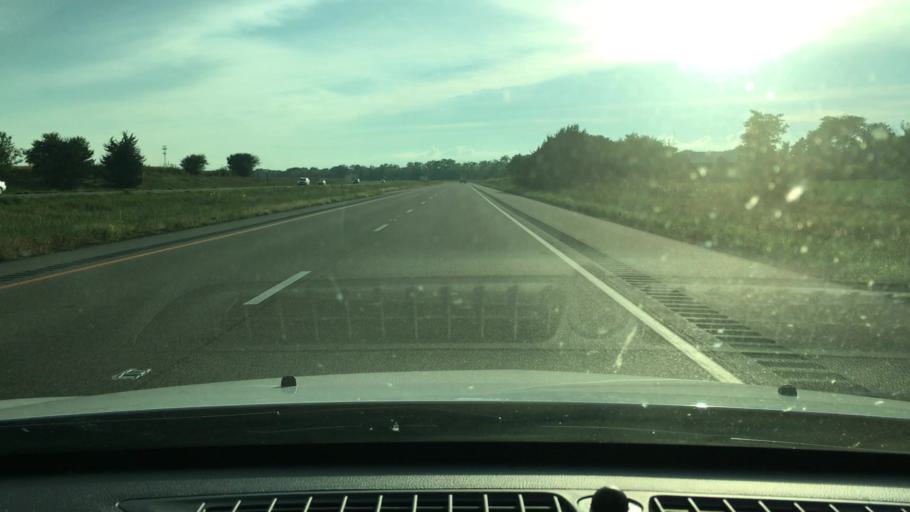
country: US
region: Illinois
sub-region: Logan County
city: Atlanta
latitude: 40.2516
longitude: -89.2352
